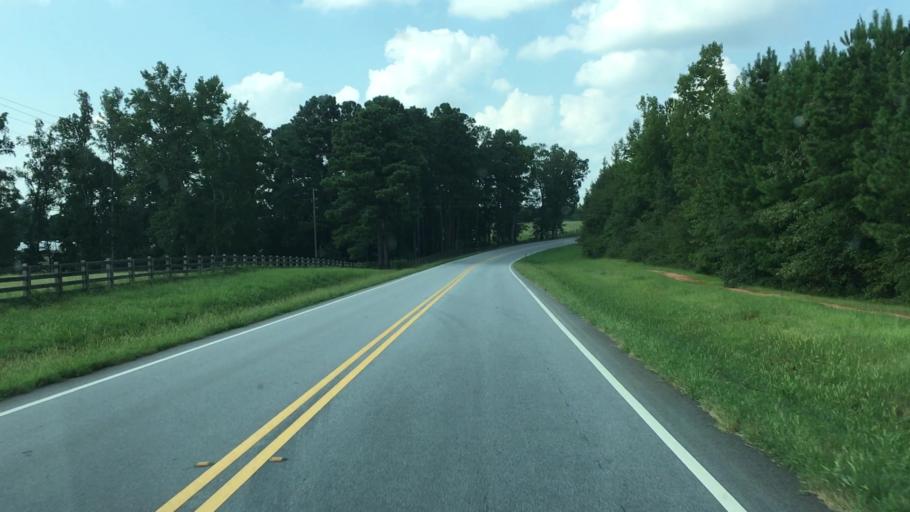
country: US
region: Georgia
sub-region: Jasper County
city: Monticello
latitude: 33.3720
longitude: -83.7551
